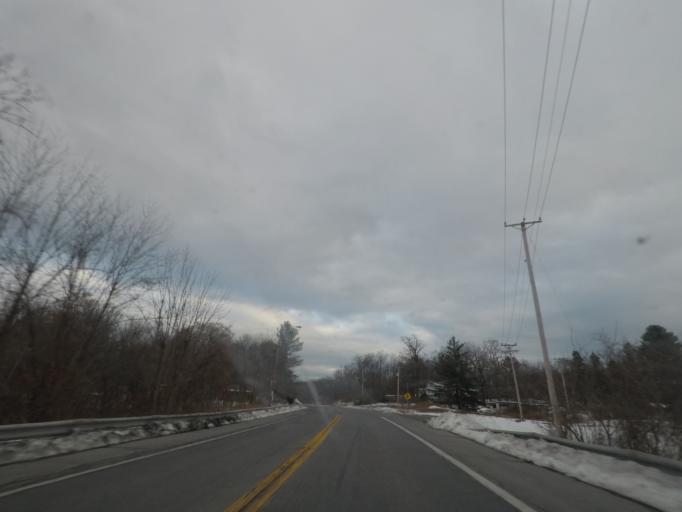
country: US
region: New York
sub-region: Ulster County
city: Plattekill
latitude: 41.6309
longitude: -74.1020
